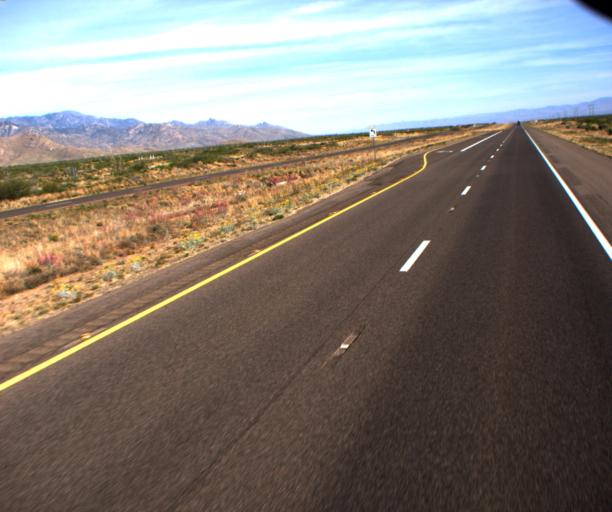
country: US
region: Arizona
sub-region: Graham County
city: Swift Trail Junction
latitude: 32.5540
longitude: -109.6780
